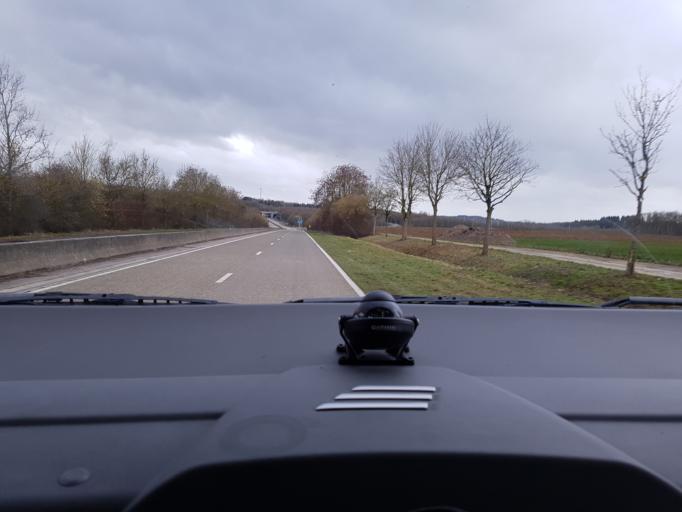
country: BE
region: Wallonia
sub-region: Province de Namur
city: Ciney
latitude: 50.2721
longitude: 5.0458
